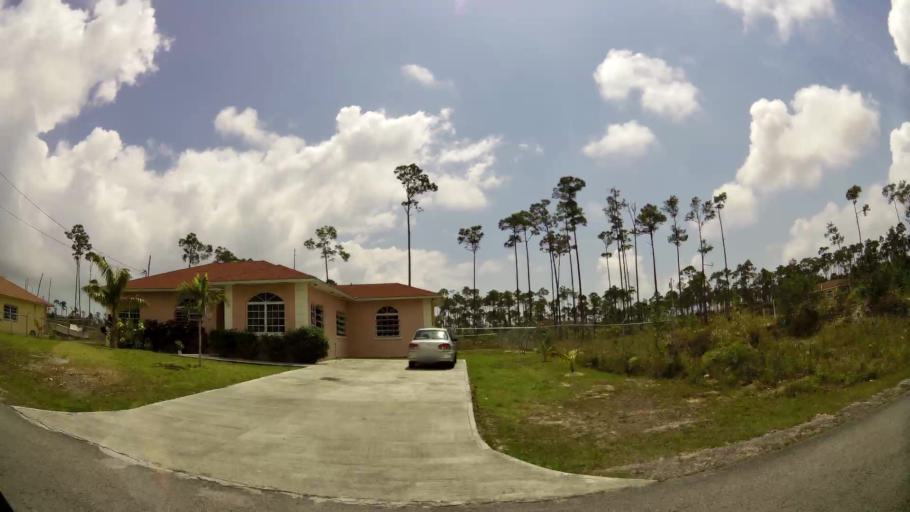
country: BS
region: Freeport
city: Lucaya
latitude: 26.5416
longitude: -78.6437
